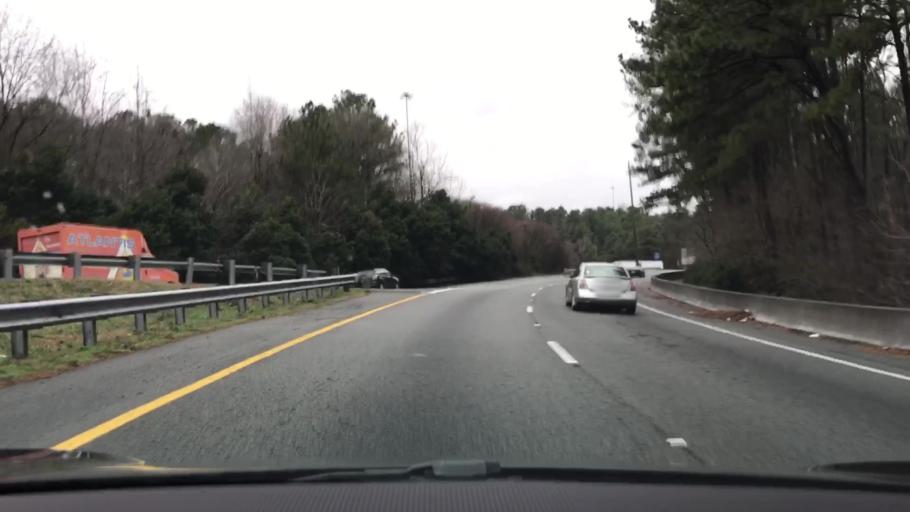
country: US
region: Georgia
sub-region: DeKalb County
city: Panthersville
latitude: 33.7155
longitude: -84.2385
